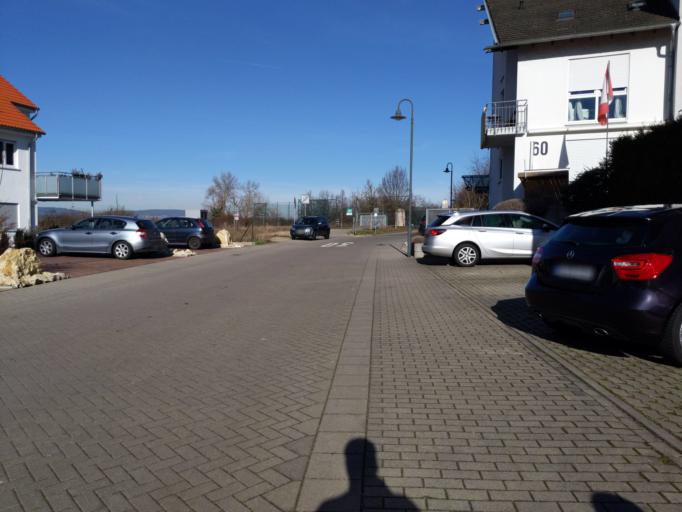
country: DE
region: Rheinland-Pfalz
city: Nieder-Ingelheim
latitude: 49.9806
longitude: 8.0781
